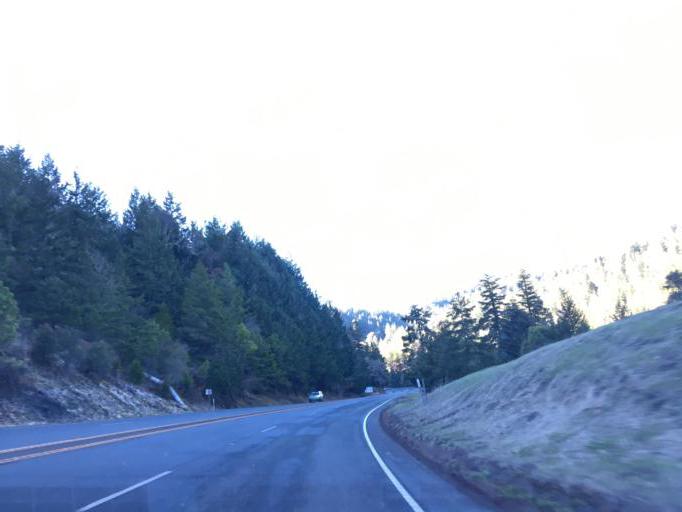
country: US
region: California
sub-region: Mendocino County
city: Laytonville
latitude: 39.8263
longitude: -123.5949
